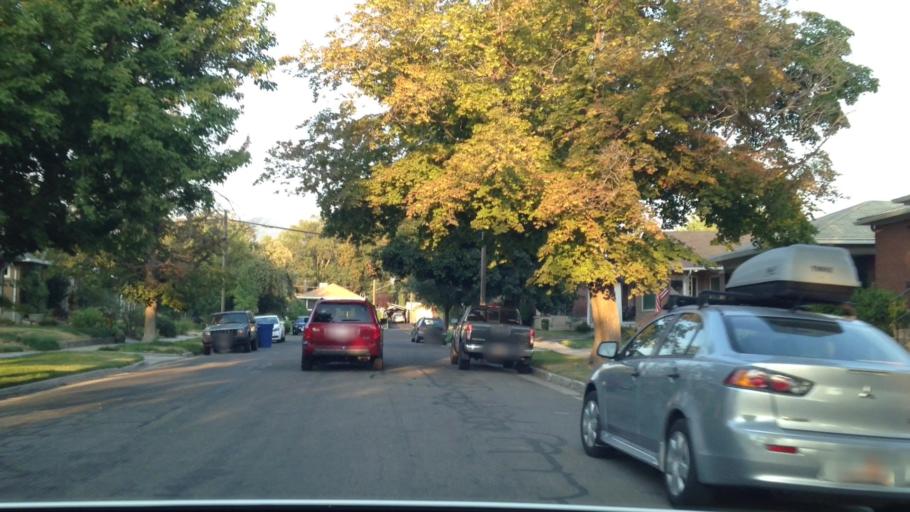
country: US
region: Utah
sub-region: Salt Lake County
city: South Salt Lake
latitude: 40.7272
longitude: -111.8753
